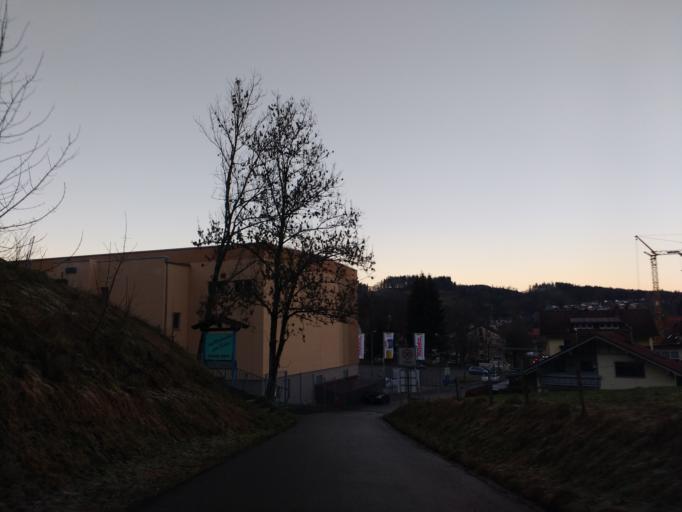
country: DE
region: Bavaria
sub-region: Swabia
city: Immenstadt im Allgau
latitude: 47.5547
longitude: 10.2192
